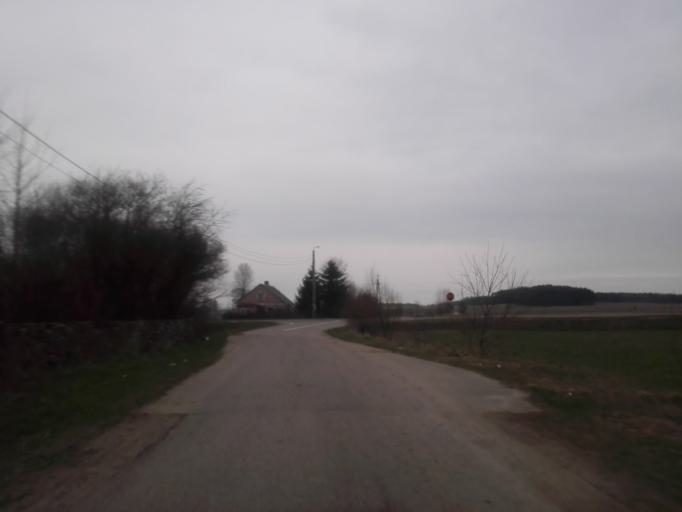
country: PL
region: Podlasie
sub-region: Powiat grajewski
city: Szczuczyn
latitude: 53.4877
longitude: 22.2196
